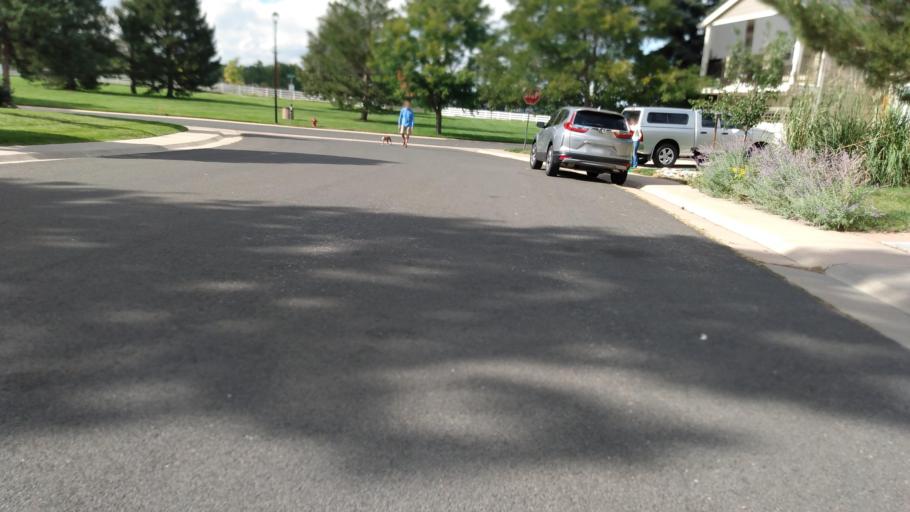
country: US
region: Colorado
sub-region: Boulder County
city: Louisville
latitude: 39.9677
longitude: -105.1408
